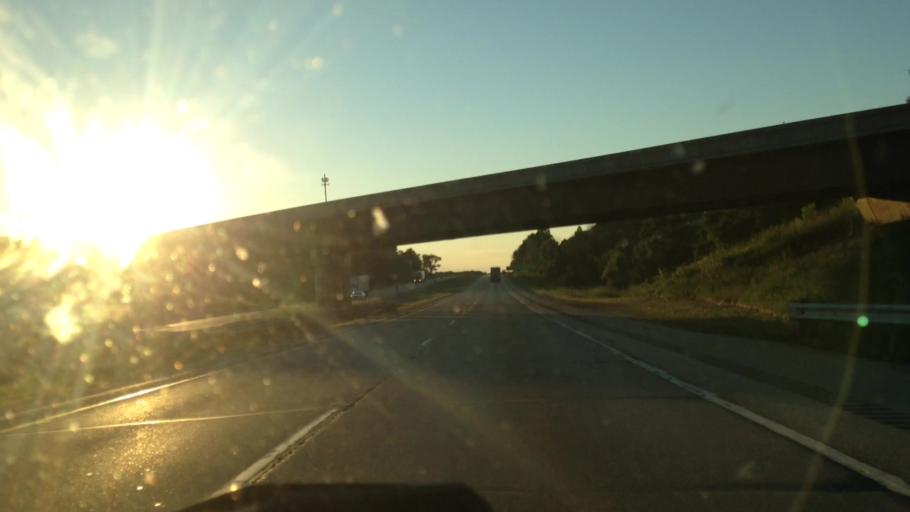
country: US
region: Wisconsin
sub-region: Washington County
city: Slinger
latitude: 43.3386
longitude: -88.2700
